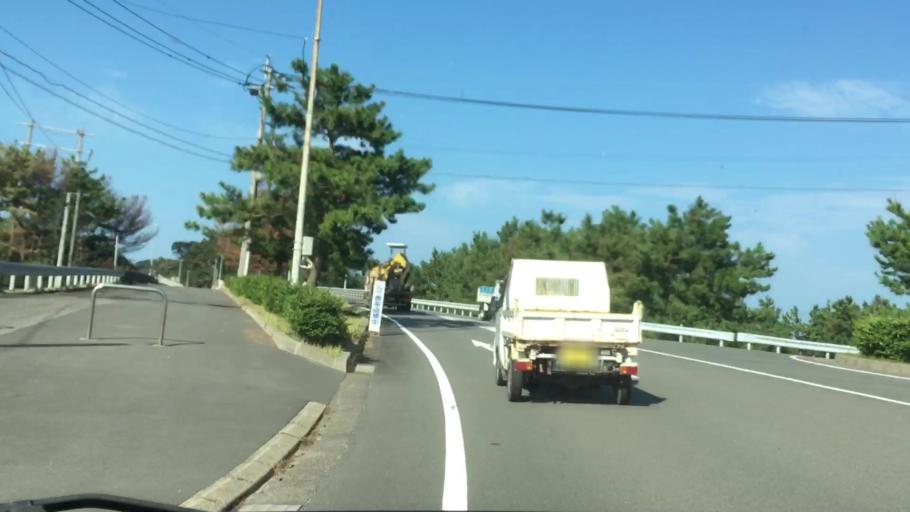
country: JP
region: Nagasaki
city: Sasebo
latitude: 33.0285
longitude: 129.5882
